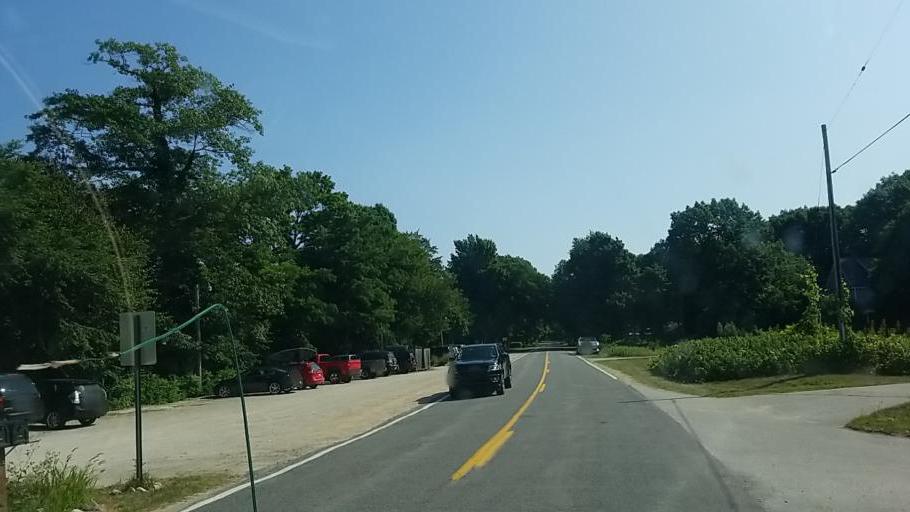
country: US
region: Michigan
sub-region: Muskegon County
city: Montague
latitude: 43.3628
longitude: -86.4075
